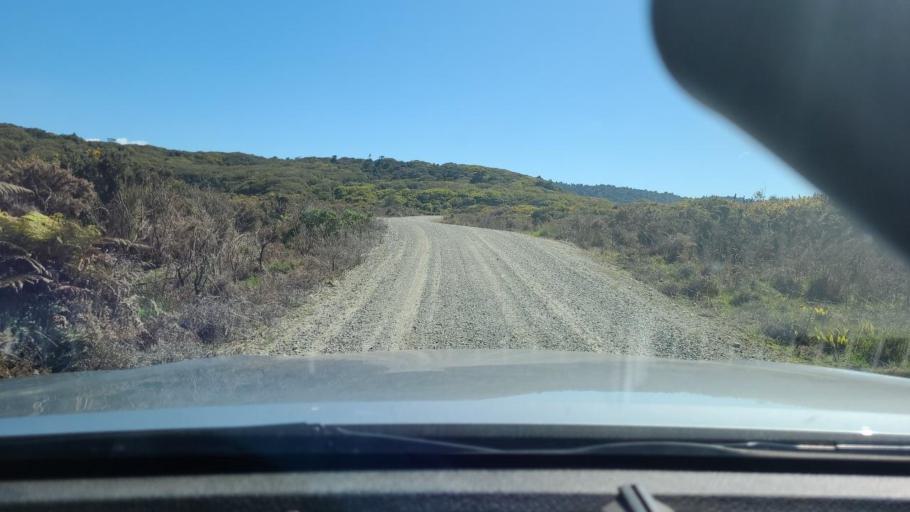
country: NZ
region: Southland
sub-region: Southland District
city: Riverton
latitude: -46.1504
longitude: 167.5103
